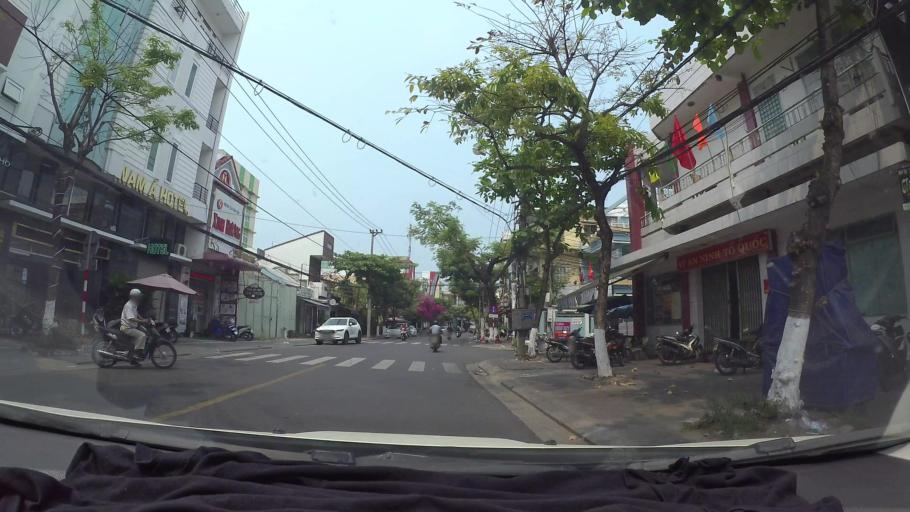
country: VN
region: Da Nang
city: Da Nang
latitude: 16.0564
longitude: 108.2202
